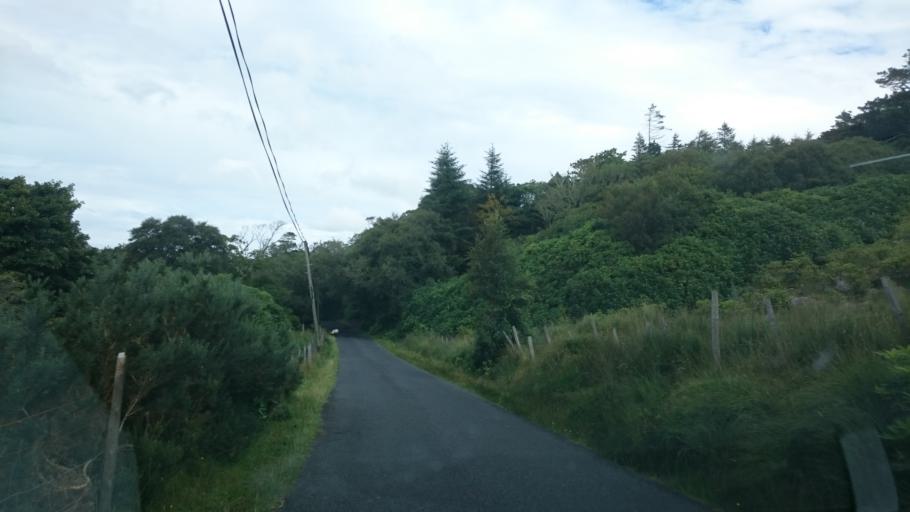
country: IE
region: Connaught
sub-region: Maigh Eo
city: Westport
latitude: 53.9484
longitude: -9.5663
